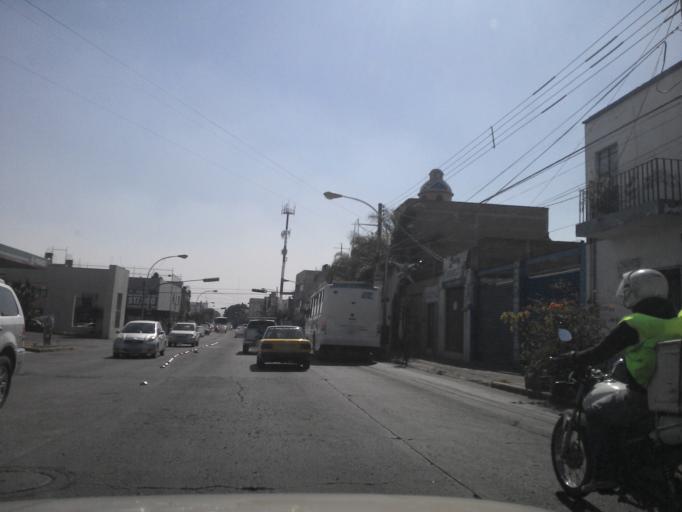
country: MX
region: Jalisco
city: Guadalajara
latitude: 20.6892
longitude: -103.3590
